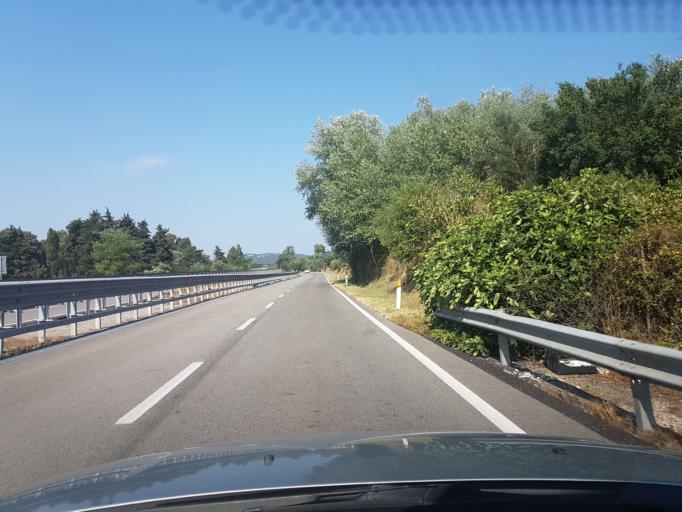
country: IT
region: Sardinia
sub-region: Provincia di Nuoro
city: Oniferi
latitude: 40.3116
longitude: 9.2103
